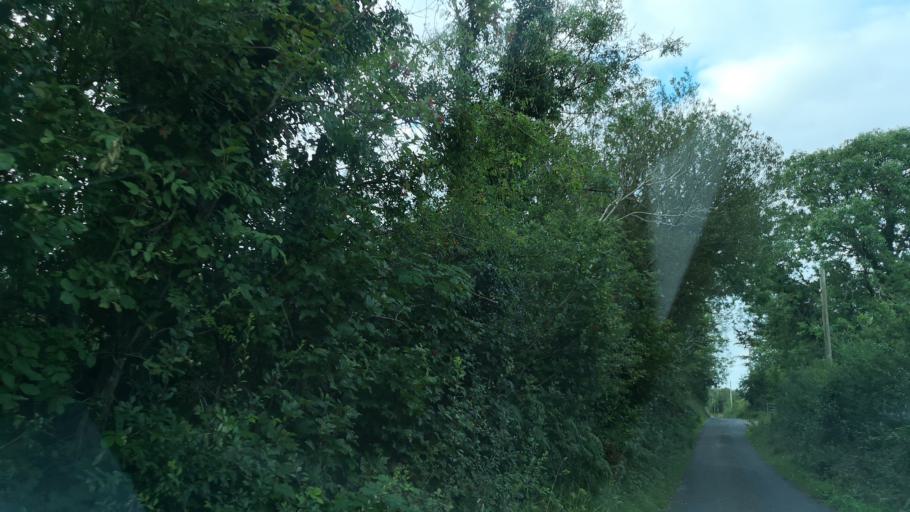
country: IE
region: Connaught
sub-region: County Galway
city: Loughrea
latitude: 53.1468
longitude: -8.5167
